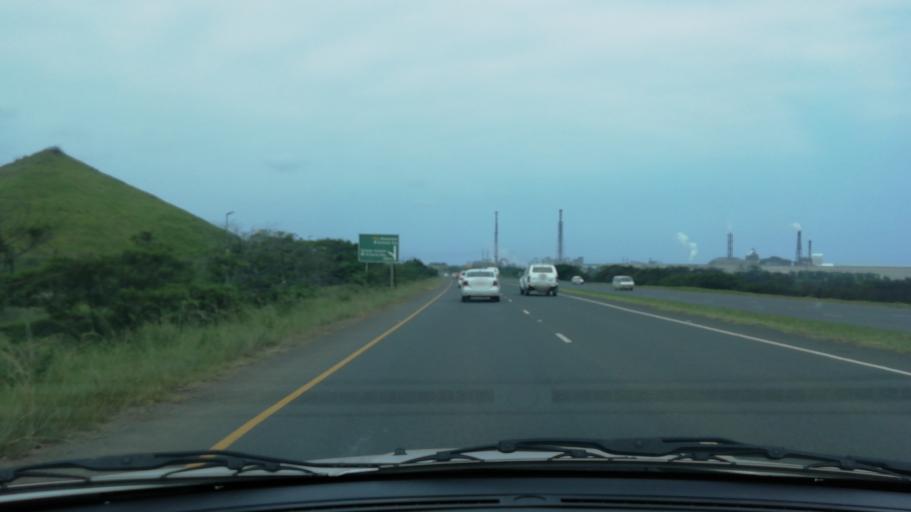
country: ZA
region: KwaZulu-Natal
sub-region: uThungulu District Municipality
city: Richards Bay
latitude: -28.7718
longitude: 32.0249
